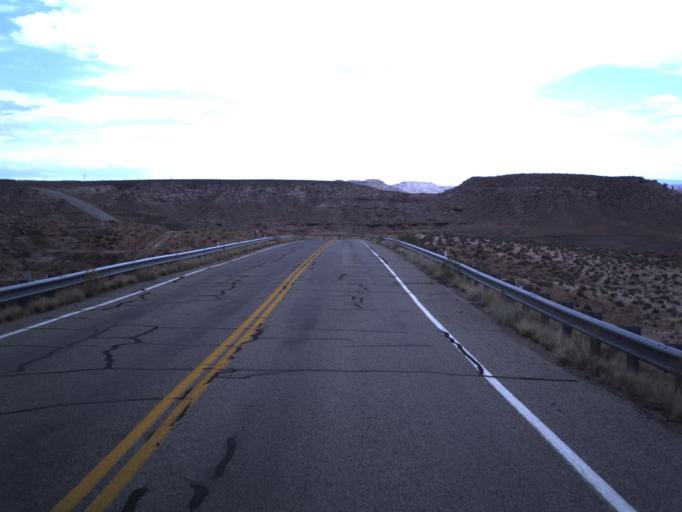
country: US
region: Utah
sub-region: San Juan County
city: Blanding
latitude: 37.2851
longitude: -109.3860
